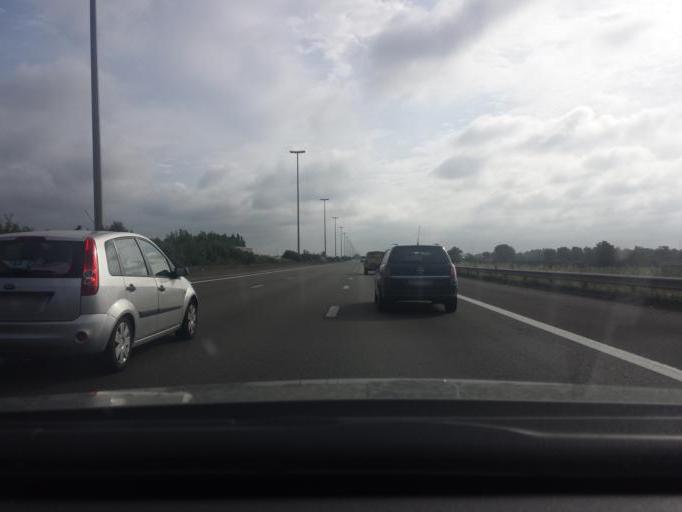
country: BE
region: Flanders
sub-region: Provincie West-Vlaanderen
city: Zwevegem
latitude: 50.8311
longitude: 3.3274
